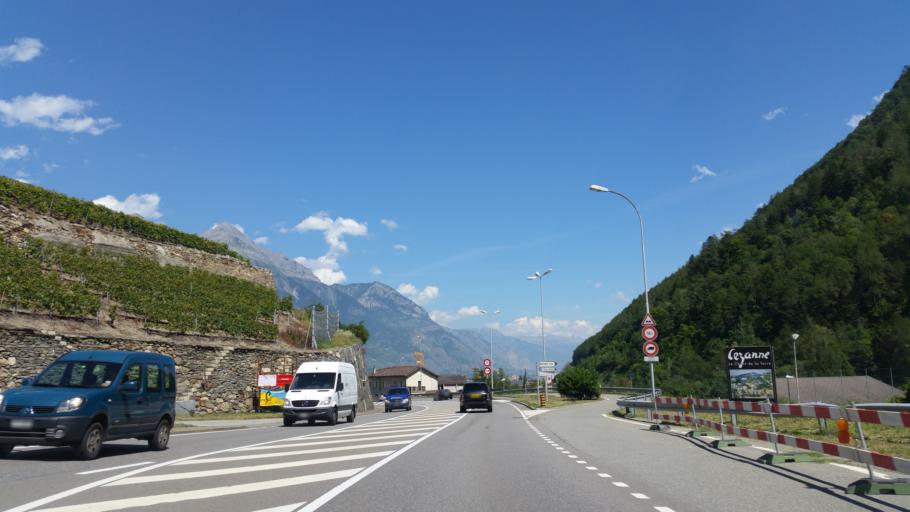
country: CH
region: Valais
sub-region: Martigny District
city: Martigny-Combe
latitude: 46.0836
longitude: 7.0534
